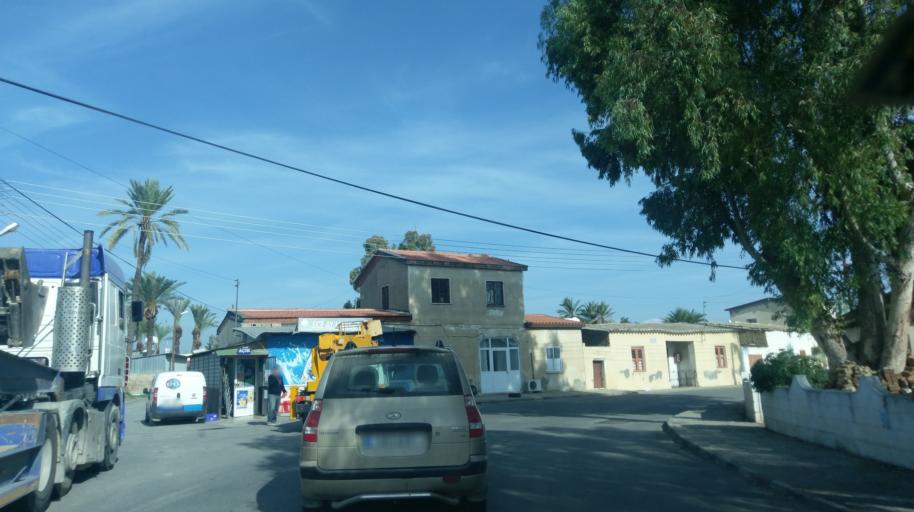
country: CY
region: Ammochostos
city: Lefkonoiko
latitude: 35.1662
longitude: 33.6388
